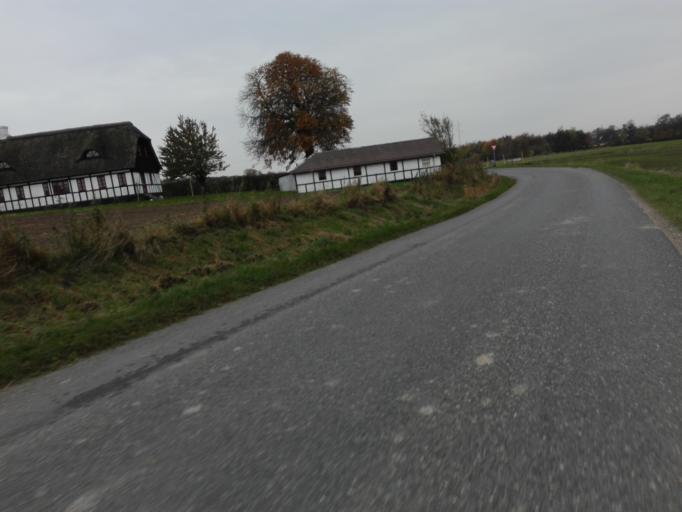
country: DK
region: Central Jutland
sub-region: Arhus Kommune
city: Beder
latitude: 56.0484
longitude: 10.2199
